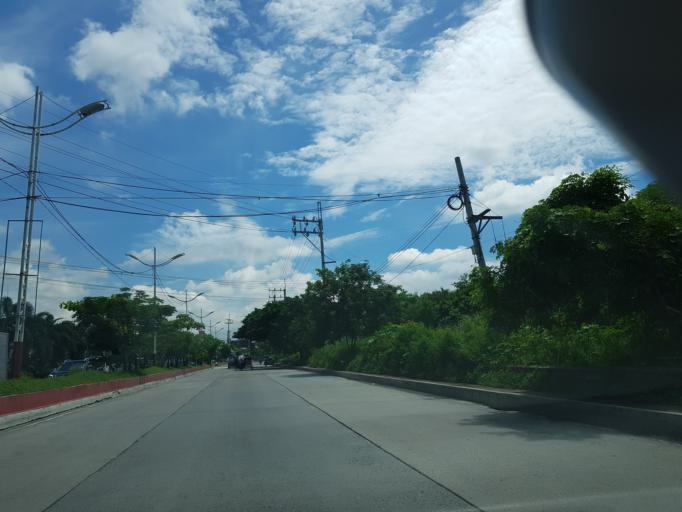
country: PH
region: Calabarzon
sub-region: Province of Rizal
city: Pateros
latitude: 14.5308
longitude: 121.0663
